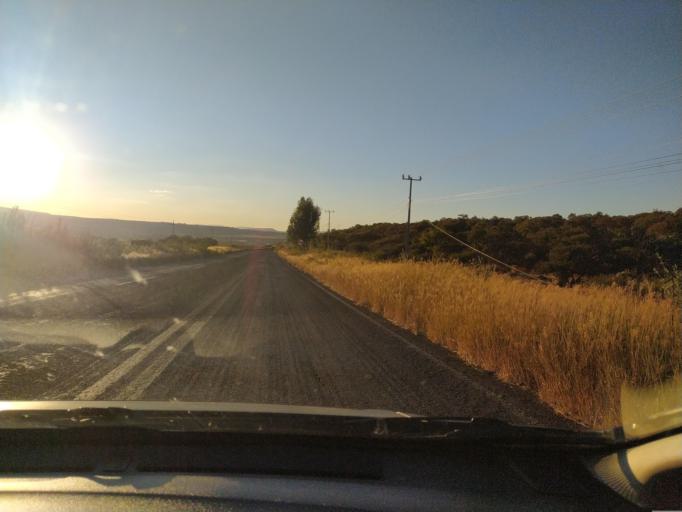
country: MX
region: Jalisco
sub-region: San Julian
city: Colonia Veintitres de Mayo
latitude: 21.0087
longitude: -102.2650
